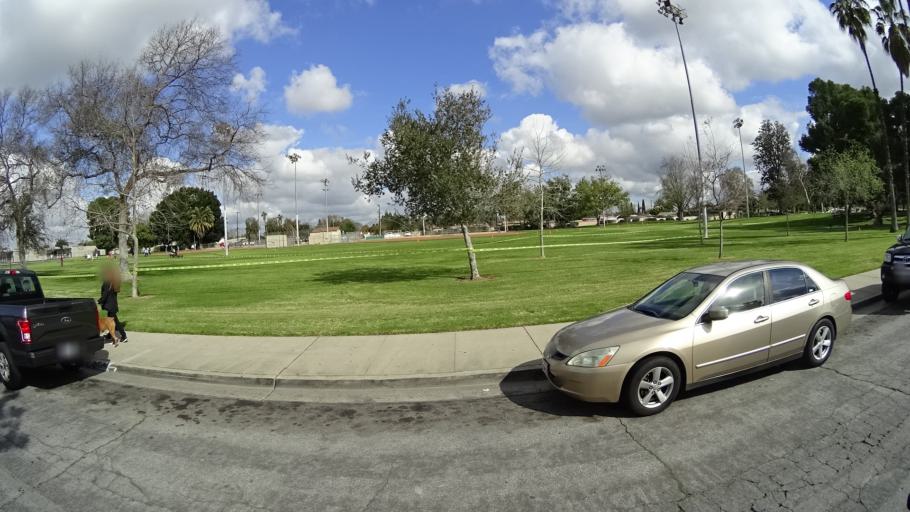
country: US
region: California
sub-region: Orange County
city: Buena Park
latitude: 33.8420
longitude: -117.9648
